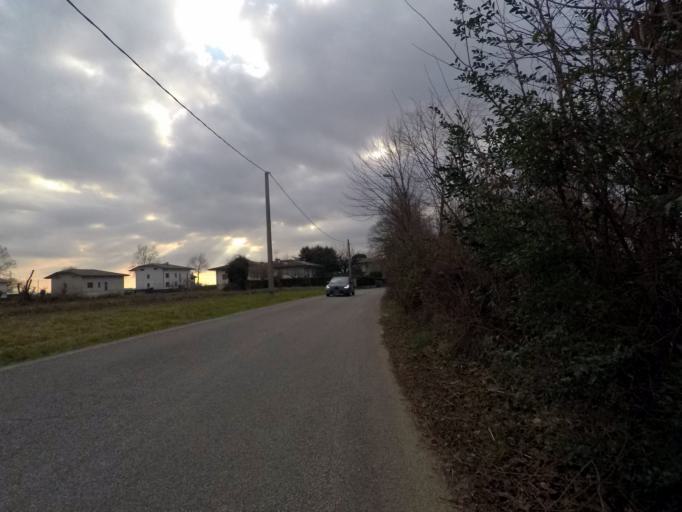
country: IT
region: Friuli Venezia Giulia
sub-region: Provincia di Udine
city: Tavagnacco
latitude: 46.1220
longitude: 13.2110
